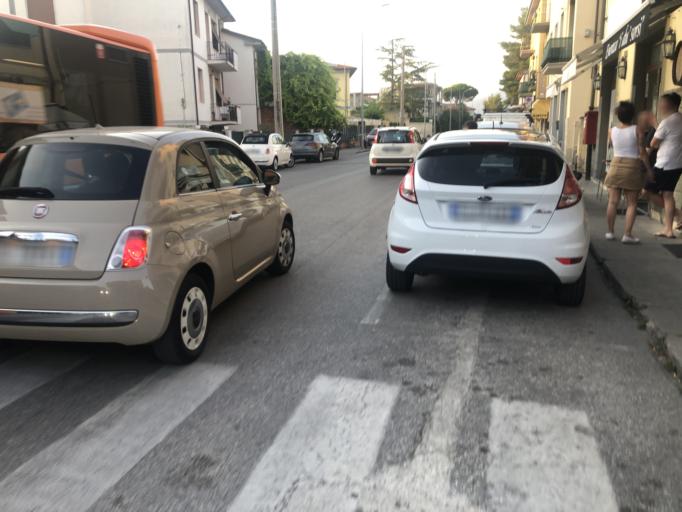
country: IT
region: Tuscany
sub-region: Province of Pisa
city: Pisa
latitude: 43.7282
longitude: 10.4060
